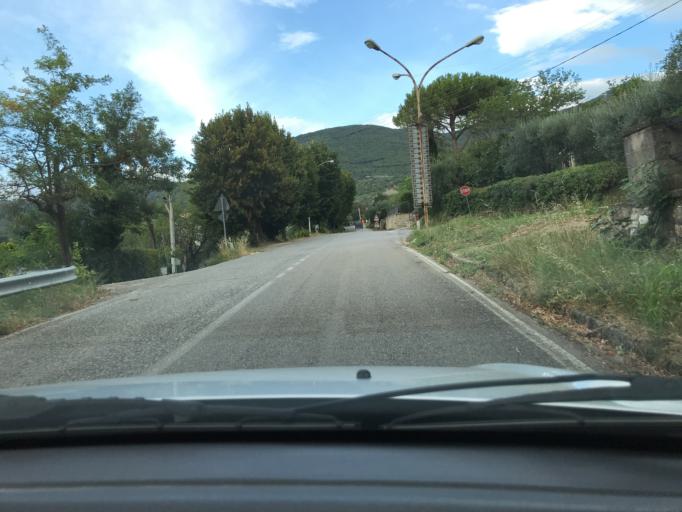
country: IT
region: Umbria
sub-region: Provincia di Terni
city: Montecchio
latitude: 42.6644
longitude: 12.2882
